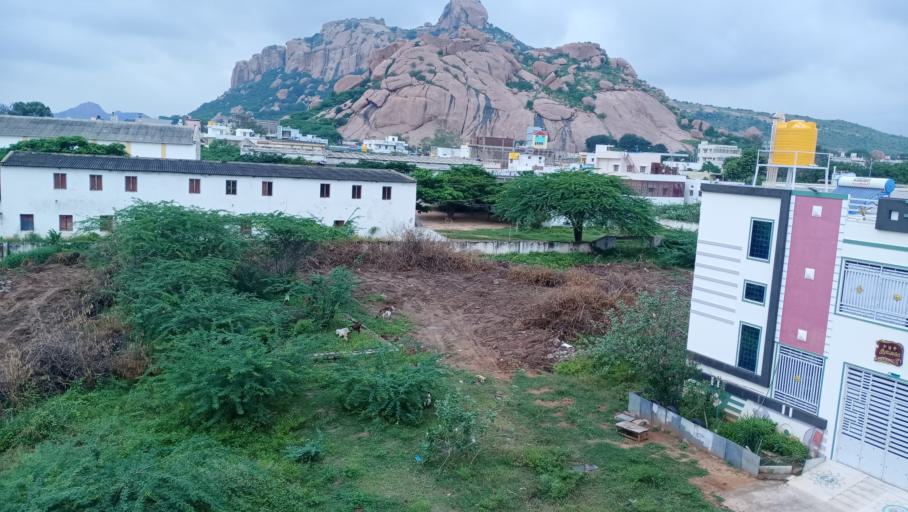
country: IN
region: Karnataka
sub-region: Tumkur
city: Pavagada
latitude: 13.9403
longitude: 77.2788
